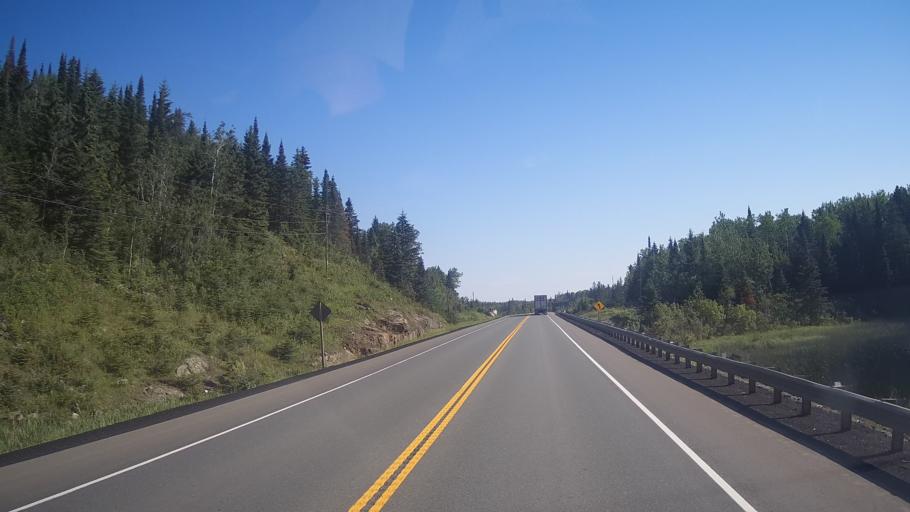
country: CA
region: Ontario
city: Dryden
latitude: 49.6260
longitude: -92.4418
